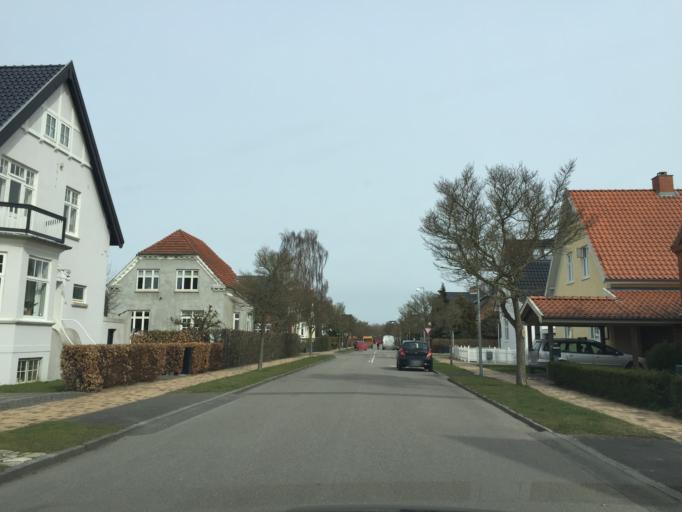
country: DK
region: South Denmark
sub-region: Odense Kommune
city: Odense
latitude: 55.3852
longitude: 10.3818
